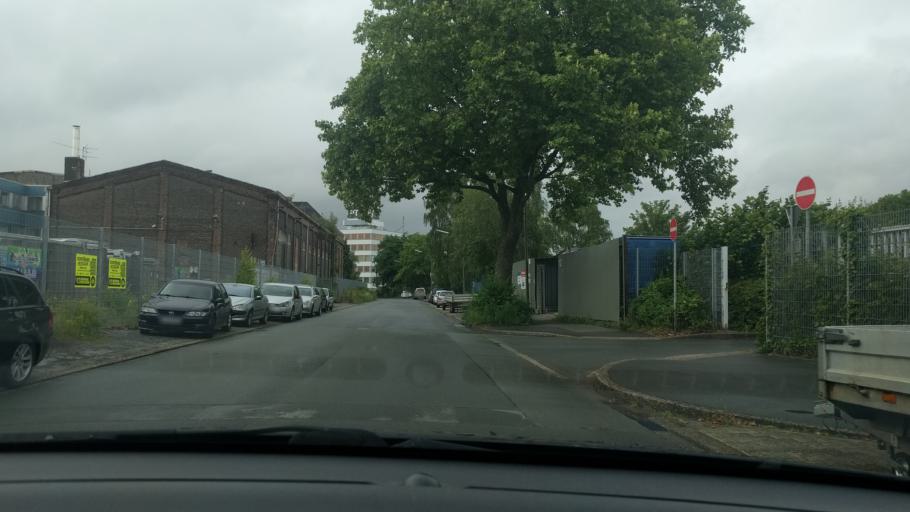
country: DE
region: North Rhine-Westphalia
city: Witten
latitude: 51.4916
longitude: 7.3668
